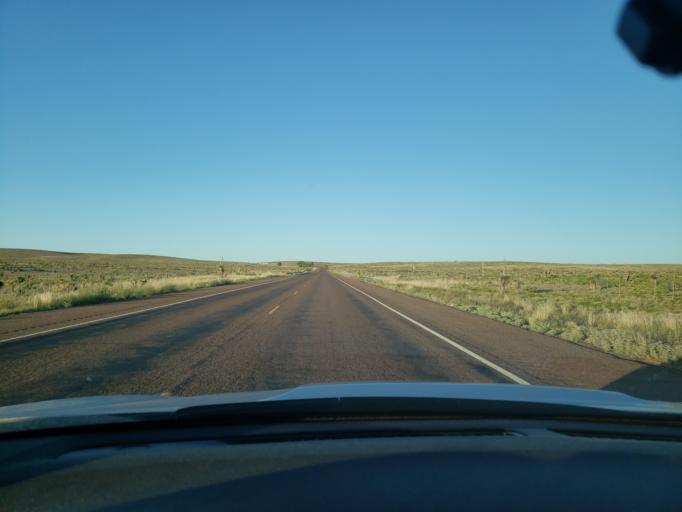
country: US
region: Texas
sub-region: El Paso County
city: Homestead Meadows South
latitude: 31.8346
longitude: -105.8536
